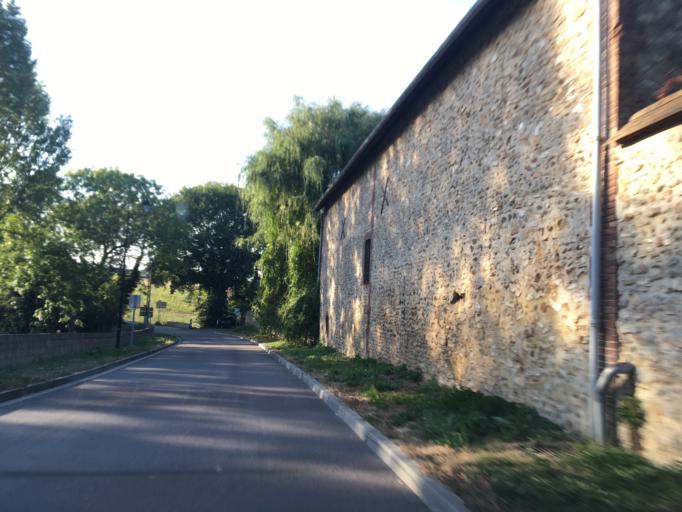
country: FR
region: Haute-Normandie
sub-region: Departement de l'Eure
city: Saint-Aubin-sur-Gaillon
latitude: 49.1374
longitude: 1.3003
